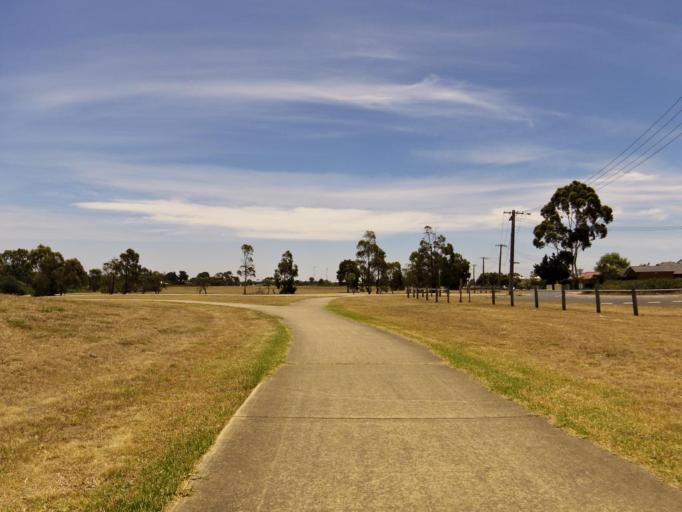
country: AU
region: Victoria
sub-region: Hobsons Bay
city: Laverton
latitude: -37.8765
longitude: 144.7665
